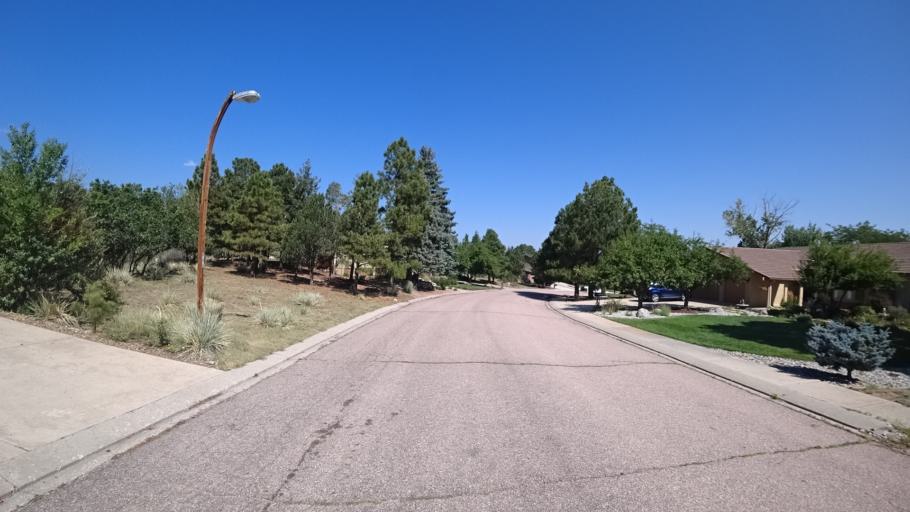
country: US
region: Colorado
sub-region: El Paso County
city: Air Force Academy
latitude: 38.9274
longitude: -104.8276
